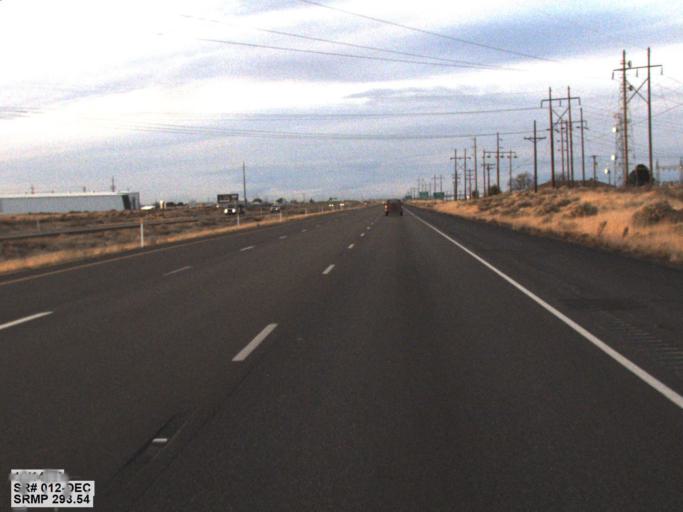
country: US
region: Washington
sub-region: Walla Walla County
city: Burbank
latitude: 46.2279
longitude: -119.0398
